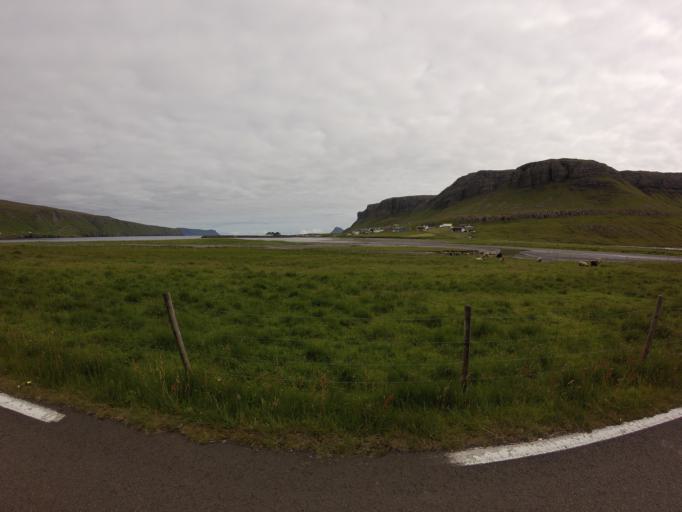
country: FO
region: Suduroy
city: Tvoroyri
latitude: 61.5909
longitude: -6.9418
